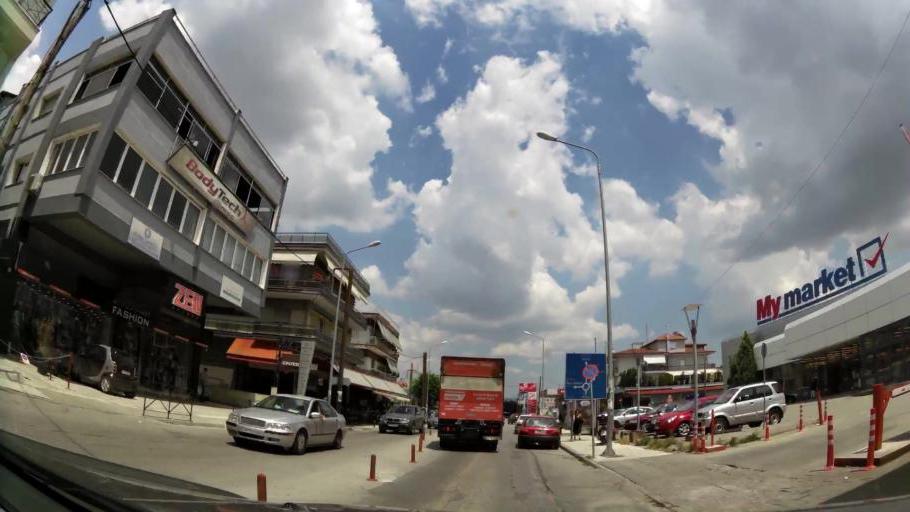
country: GR
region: West Macedonia
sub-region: Nomos Kozanis
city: Kozani
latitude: 40.2987
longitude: 21.7975
